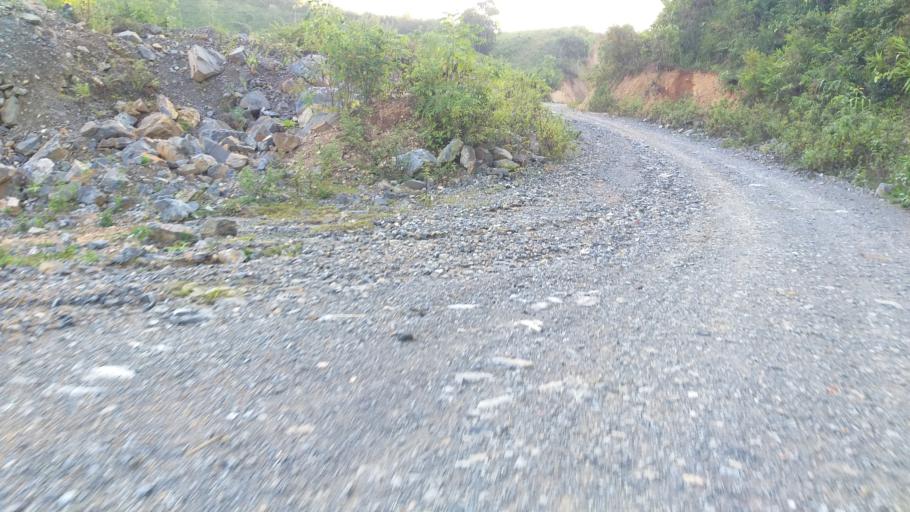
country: LA
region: Phongsali
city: Khoa
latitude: 21.2220
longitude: 102.5975
